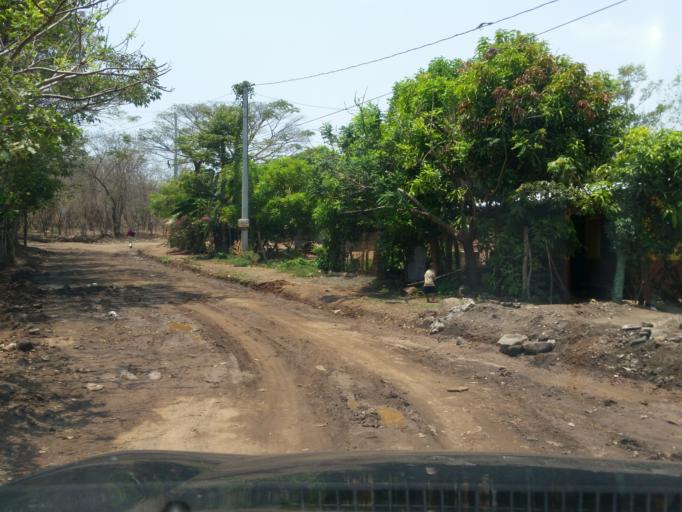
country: NI
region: Granada
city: Granada
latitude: 11.9103
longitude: -85.9647
